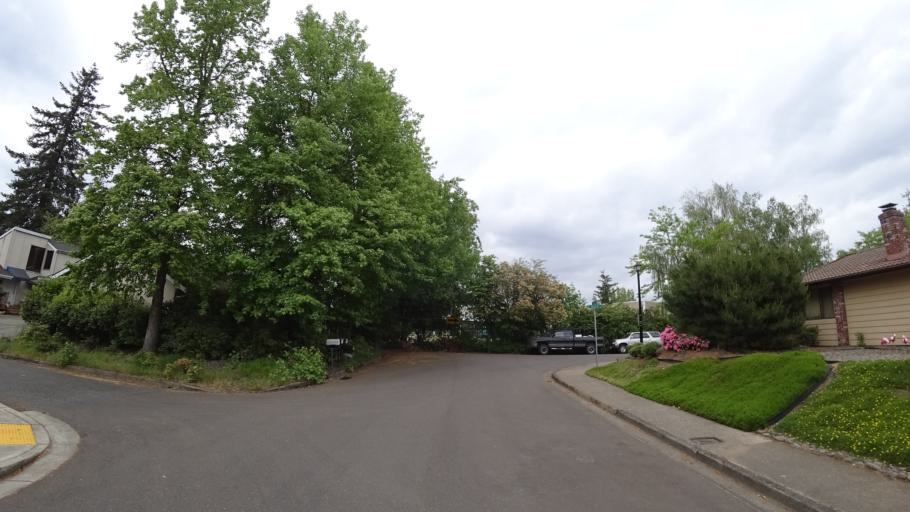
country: US
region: Oregon
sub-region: Washington County
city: Garden Home-Whitford
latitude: 45.4618
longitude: -122.7828
